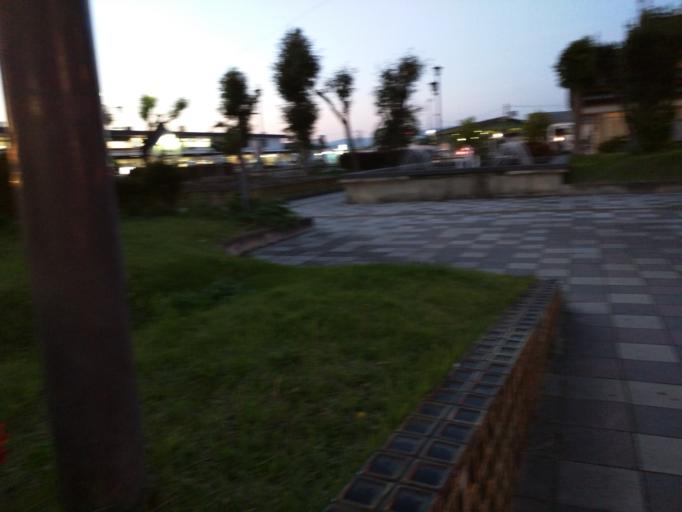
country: JP
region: Fukushima
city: Kitakata
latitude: 37.5069
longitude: 139.9311
